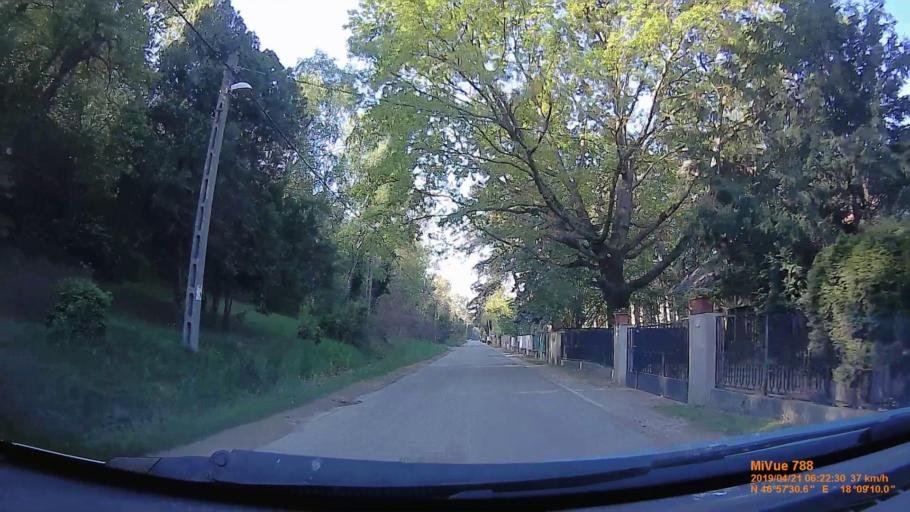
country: HU
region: Somogy
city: Balatonszabadi
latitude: 46.9585
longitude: 18.1528
